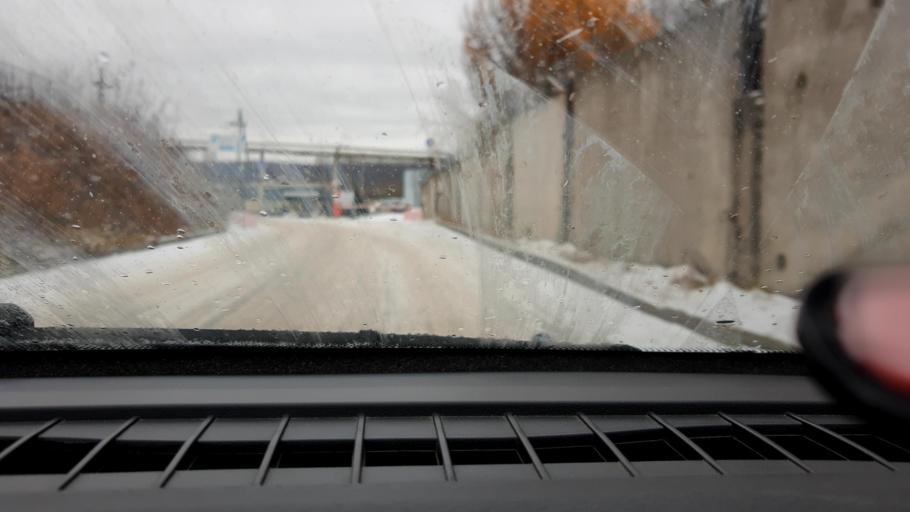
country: RU
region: Nizjnij Novgorod
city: Nizhniy Novgorod
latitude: 56.2401
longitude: 44.0022
